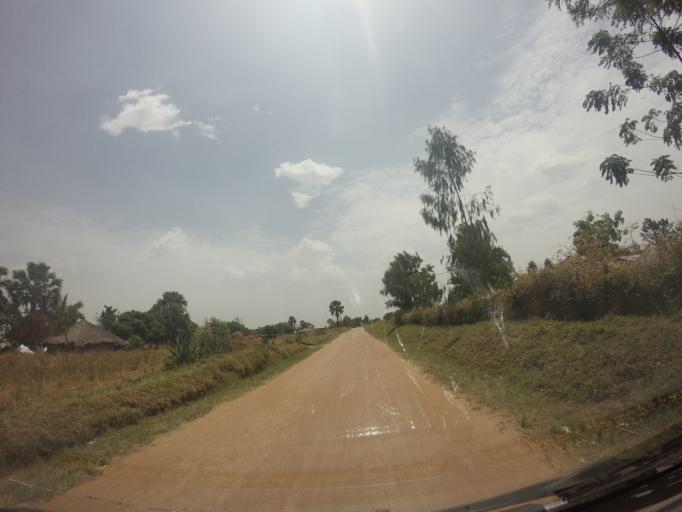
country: UG
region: Northern Region
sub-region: Arua District
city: Arua
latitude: 2.9504
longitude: 30.9138
